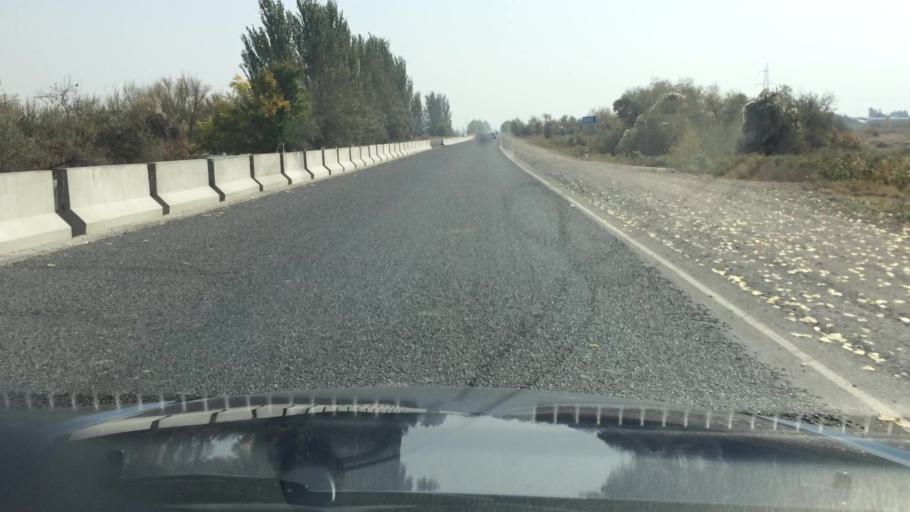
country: KG
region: Chuy
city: Kant
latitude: 42.9739
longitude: 74.8961
